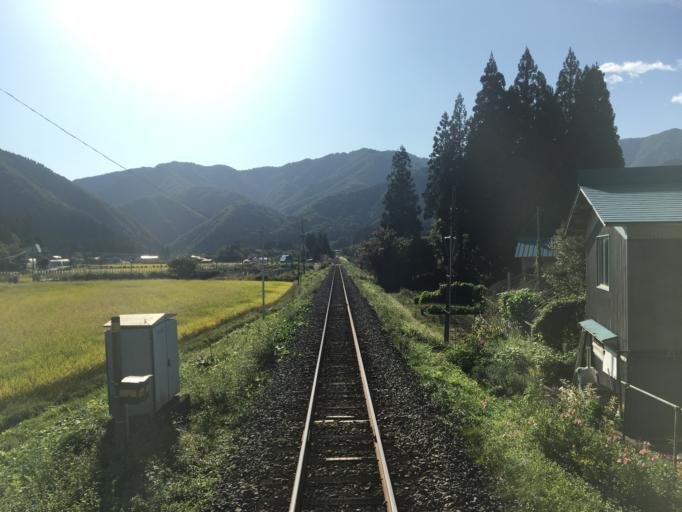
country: JP
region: Akita
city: Kakunodatemachi
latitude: 39.7287
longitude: 140.5685
